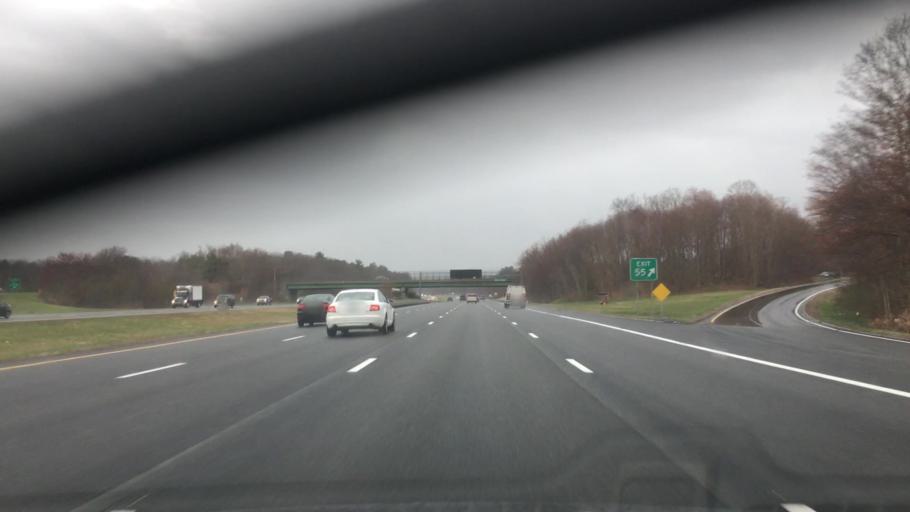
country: US
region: Massachusetts
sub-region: Essex County
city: West Newbury
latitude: 42.7589
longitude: -70.9406
